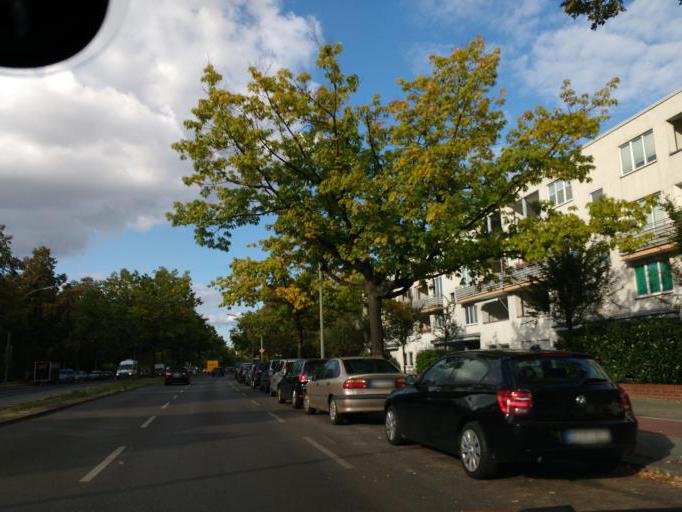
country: DE
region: Berlin
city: Britz
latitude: 52.4296
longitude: 13.4351
